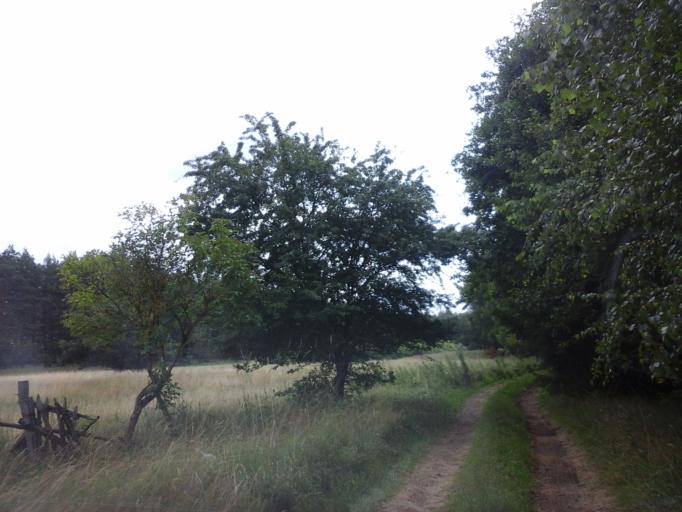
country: PL
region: West Pomeranian Voivodeship
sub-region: Powiat choszczenski
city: Pelczyce
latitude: 52.9449
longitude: 15.3493
